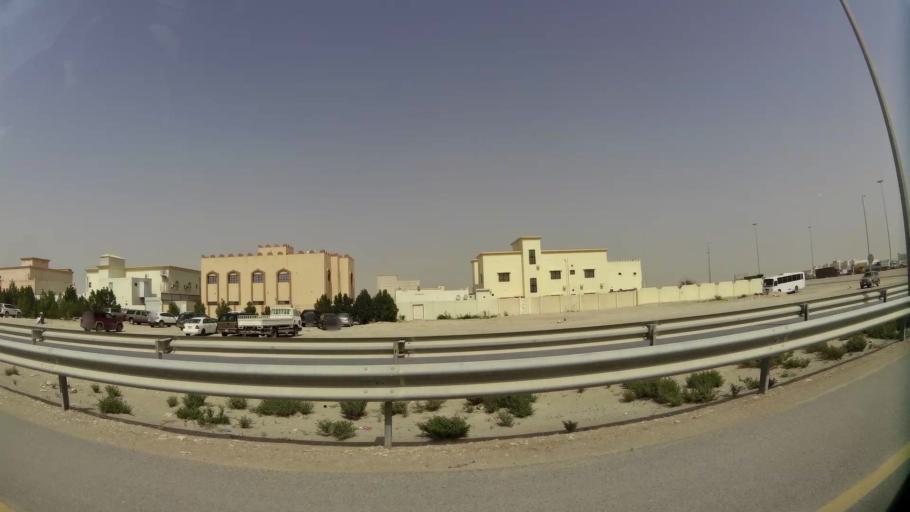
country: QA
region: Baladiyat ar Rayyan
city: Ar Rayyan
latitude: 25.1872
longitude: 51.3615
